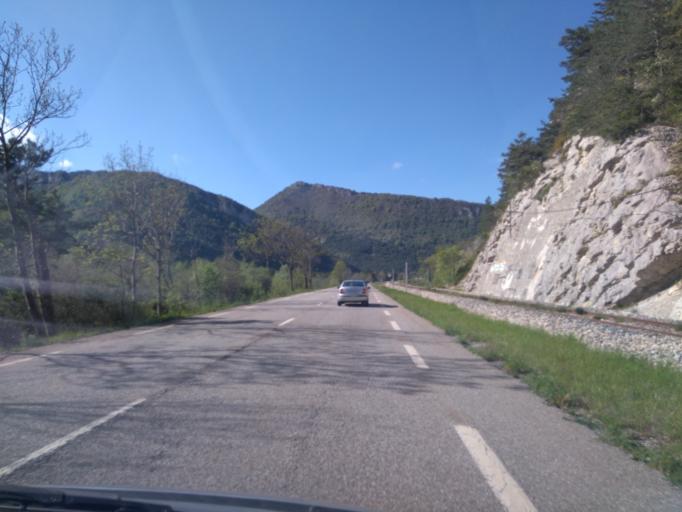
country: FR
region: Provence-Alpes-Cote d'Azur
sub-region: Departement des Hautes-Alpes
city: Veynes
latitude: 44.6286
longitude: 5.6972
